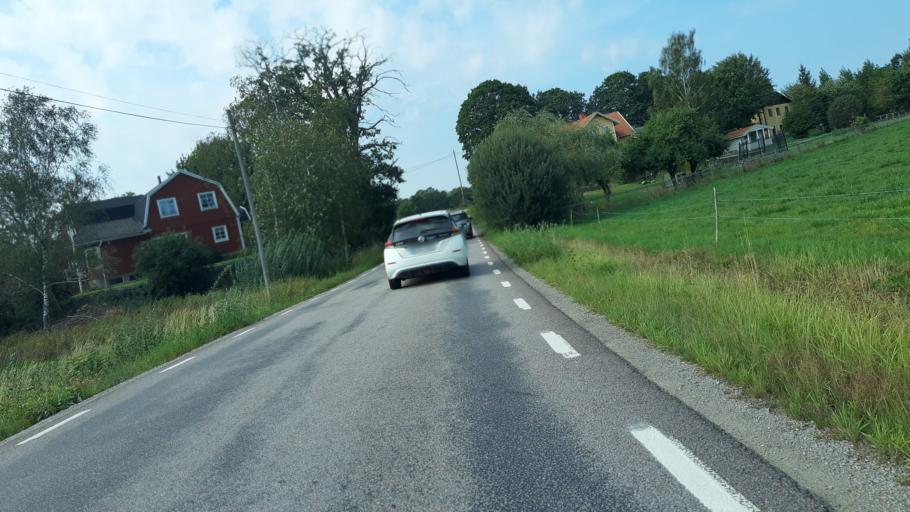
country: SE
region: Blekinge
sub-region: Karlskrona Kommun
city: Nattraby
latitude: 56.1877
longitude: 15.5260
